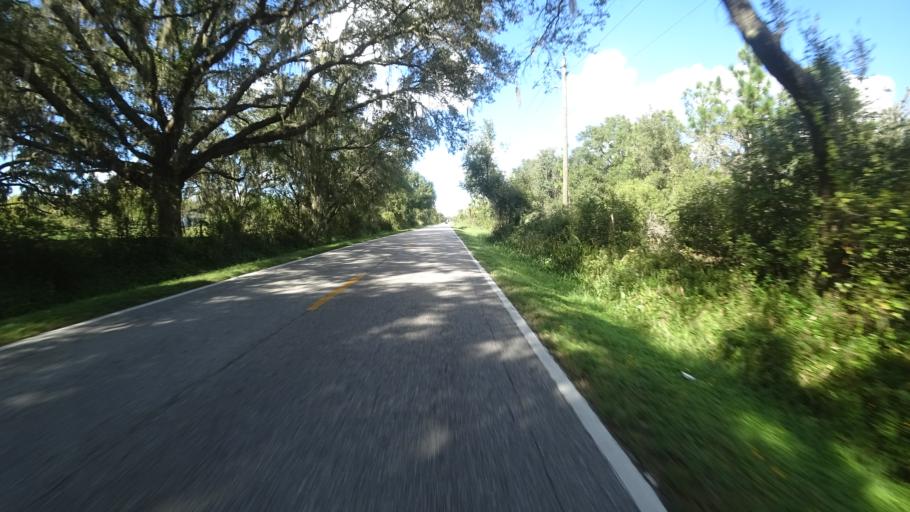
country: US
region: Florida
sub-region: Sarasota County
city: Lake Sarasota
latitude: 27.3259
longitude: -82.2694
